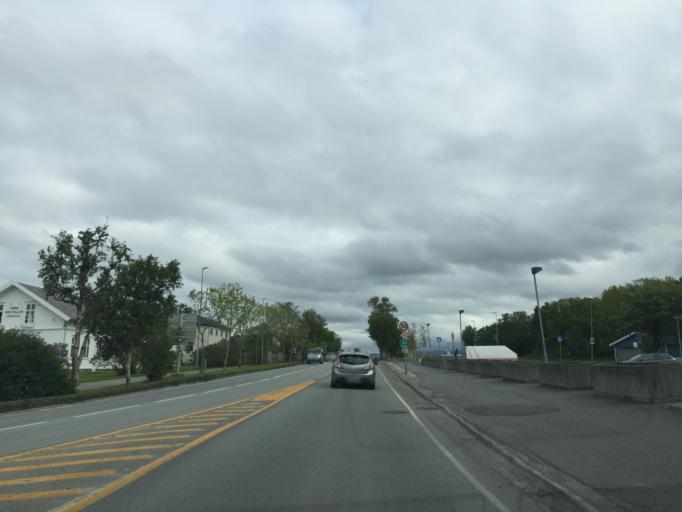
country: NO
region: Nordland
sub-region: Bodo
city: Bodo
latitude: 67.2857
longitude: 14.4018
